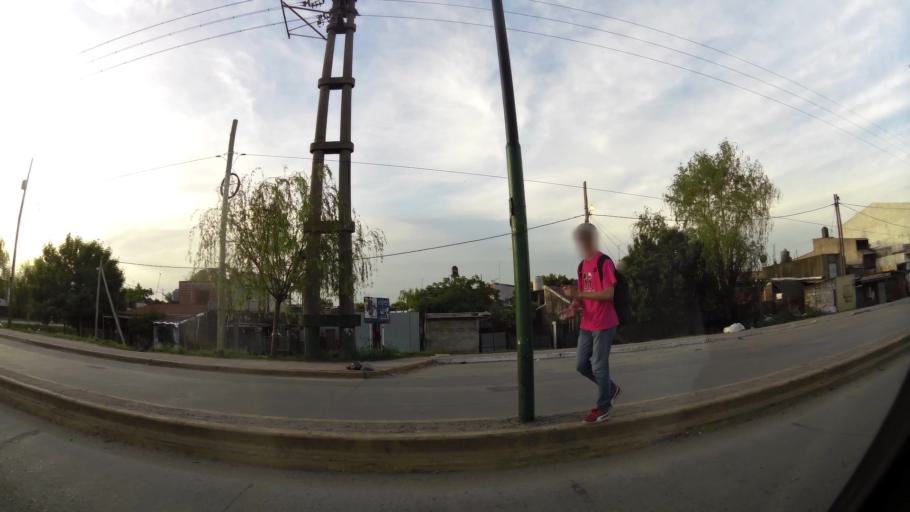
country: AR
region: Buenos Aires
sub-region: Partido de Almirante Brown
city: Adrogue
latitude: -34.7735
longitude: -58.3242
